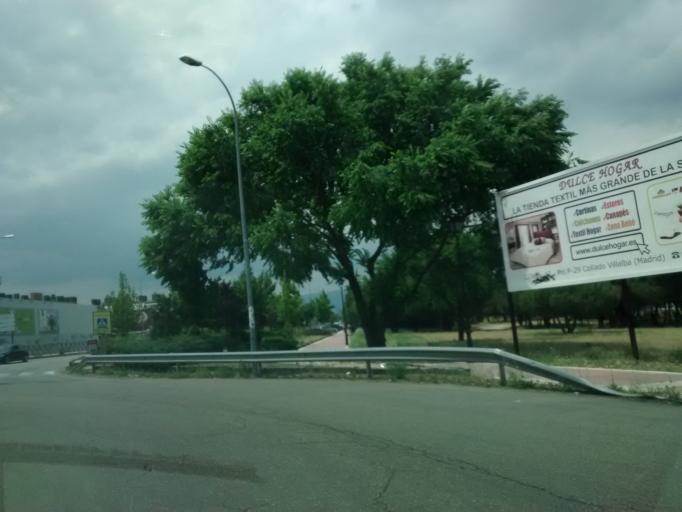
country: ES
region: Madrid
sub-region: Provincia de Madrid
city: Collado-Villalba
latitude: 40.6353
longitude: -4.0121
